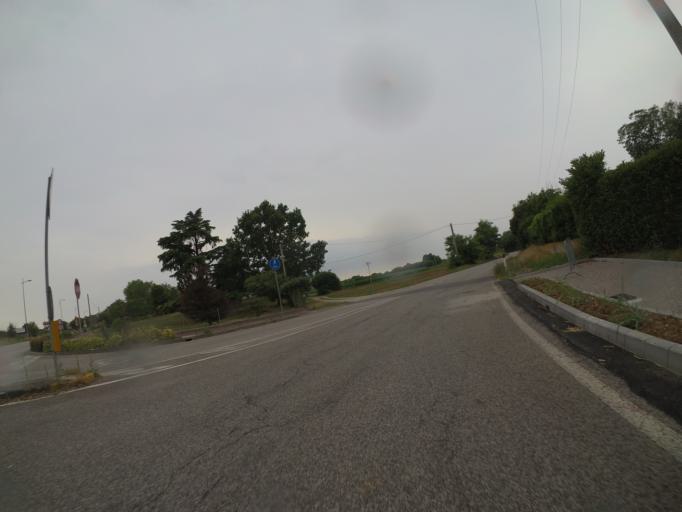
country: IT
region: Friuli Venezia Giulia
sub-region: Provincia di Udine
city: Basiliano-Vissandone
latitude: 46.0259
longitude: 13.1046
